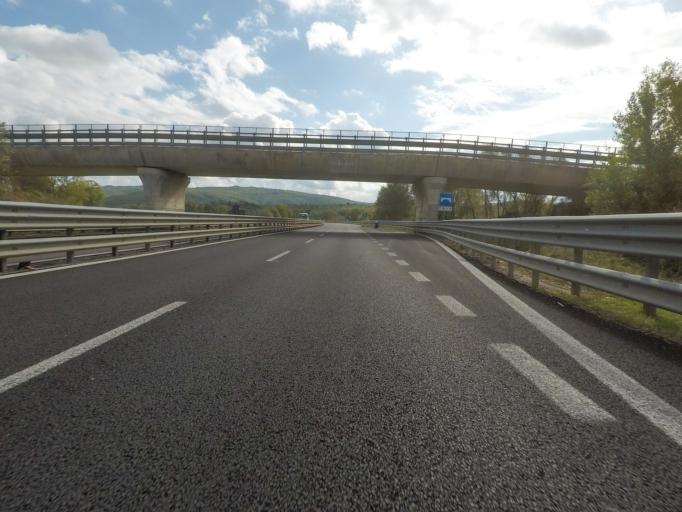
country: IT
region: Tuscany
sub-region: Provincia di Siena
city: Serre di Rapolano
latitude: 43.2487
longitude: 11.6443
